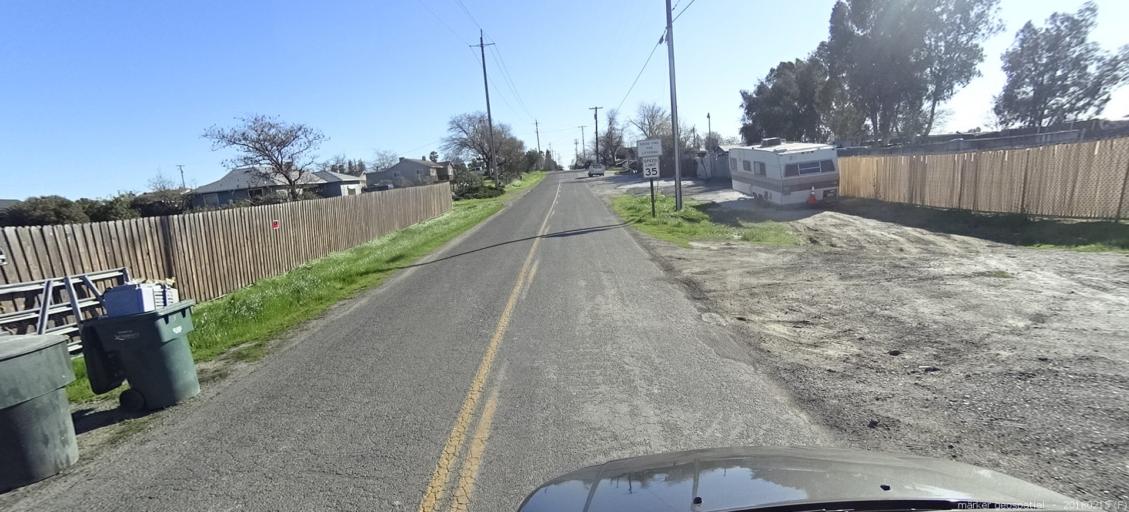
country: US
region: California
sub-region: Sacramento County
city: Elverta
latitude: 38.6909
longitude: -121.4754
